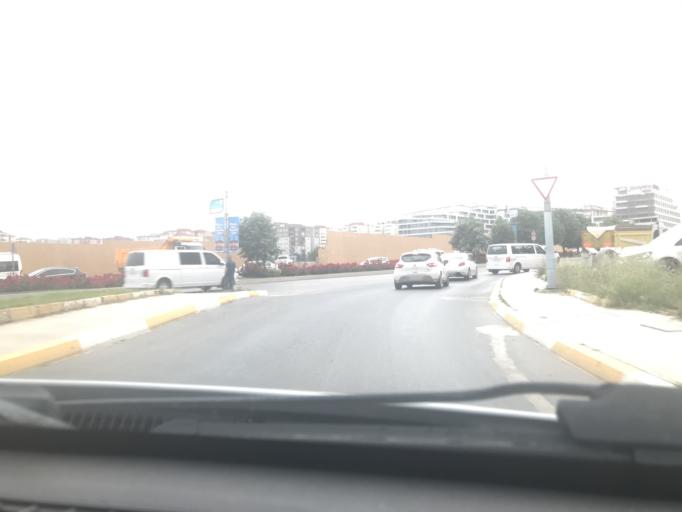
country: TR
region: Istanbul
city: Sultanbeyli
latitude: 40.9257
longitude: 29.3120
